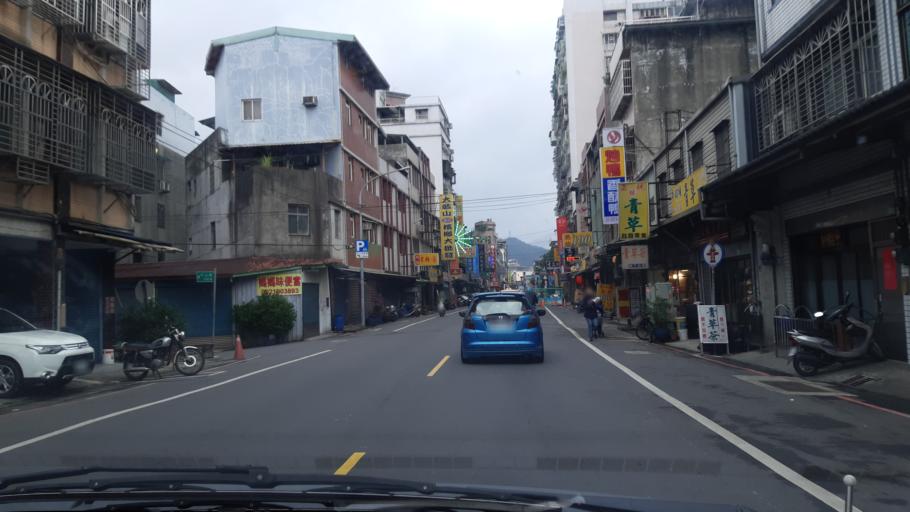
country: TW
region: Taiwan
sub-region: Taoyuan
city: Taoyuan
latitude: 24.9365
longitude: 121.3646
